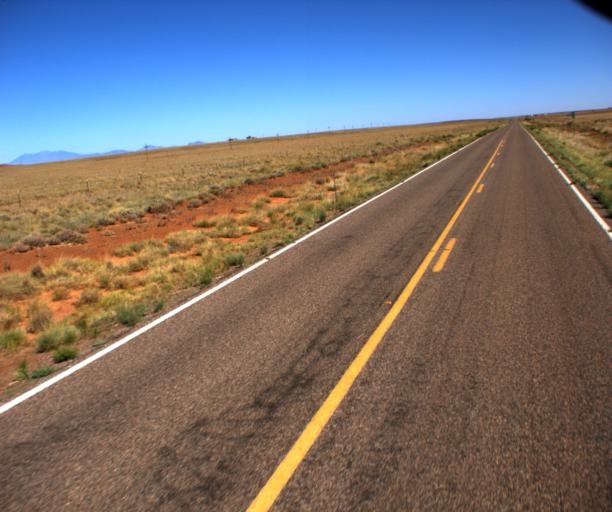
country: US
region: Arizona
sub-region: Coconino County
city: LeChee
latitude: 35.1638
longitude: -110.9123
